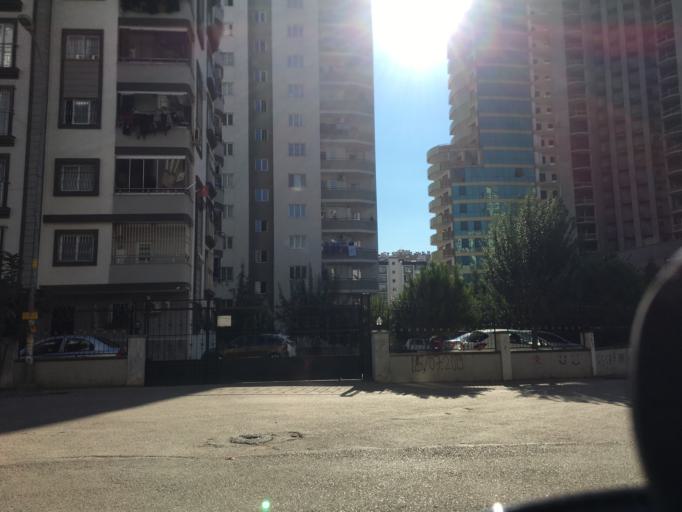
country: TR
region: Adana
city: Seyhan
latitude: 37.0224
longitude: 35.2863
